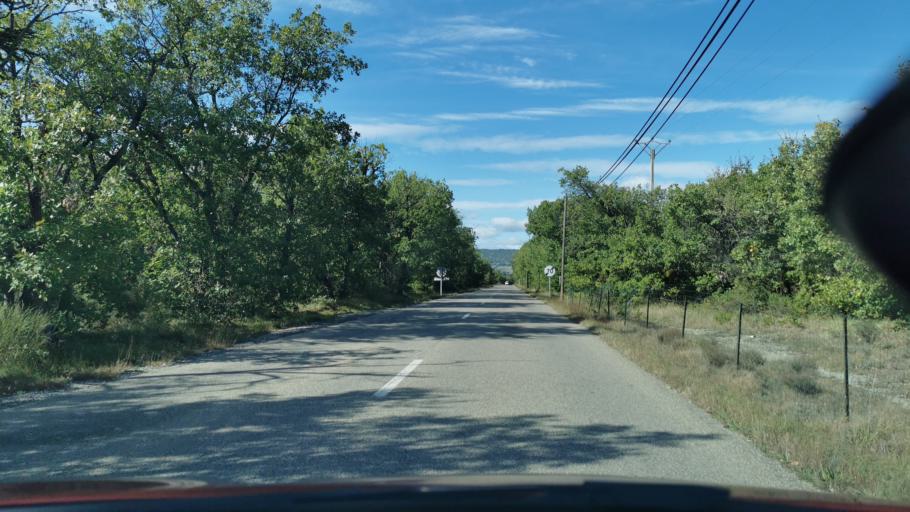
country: FR
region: Provence-Alpes-Cote d'Azur
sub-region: Departement des Alpes-de-Haute-Provence
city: Peipin
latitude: 44.1592
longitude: 5.9680
